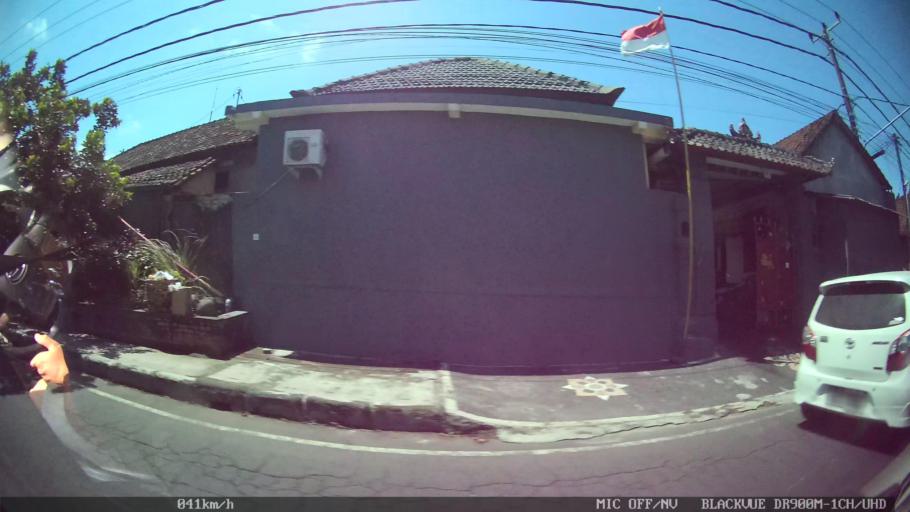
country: ID
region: Bali
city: Klungkung
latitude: -8.5640
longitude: 115.3410
